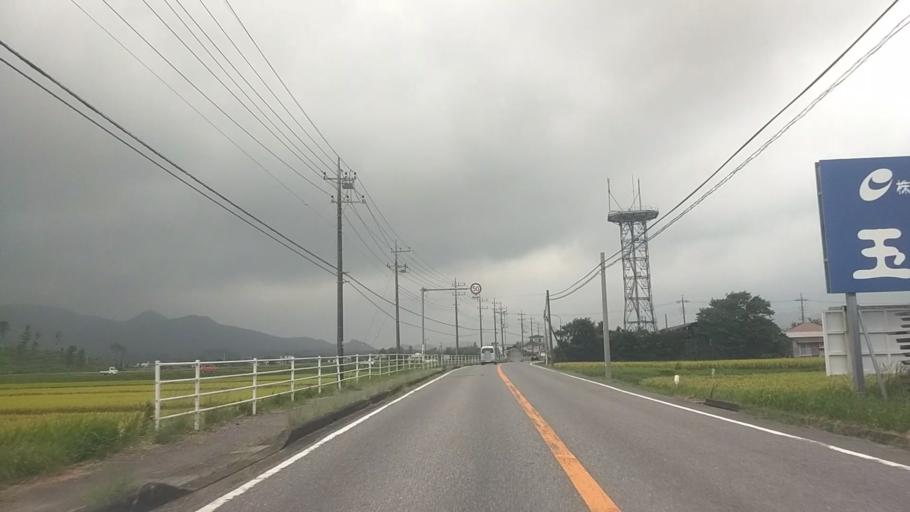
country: JP
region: Chiba
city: Kawaguchi
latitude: 35.1298
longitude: 140.0286
